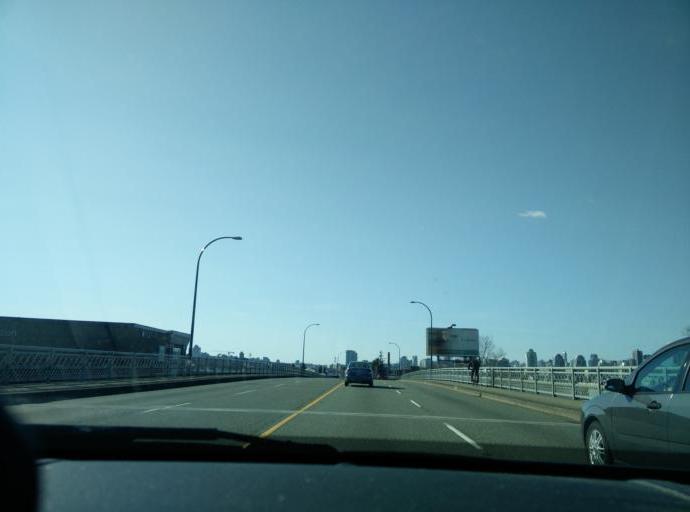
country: CA
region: British Columbia
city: Vancouver
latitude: 49.2697
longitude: -123.0796
